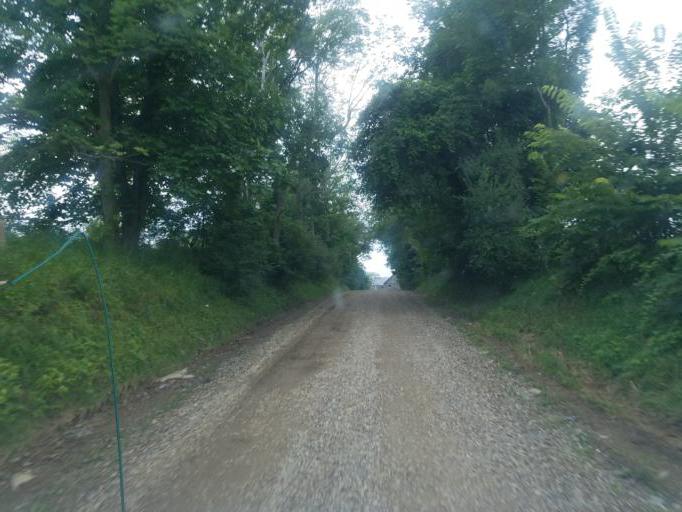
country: US
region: Ohio
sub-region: Knox County
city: Oak Hill
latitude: 40.4372
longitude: -82.1598
